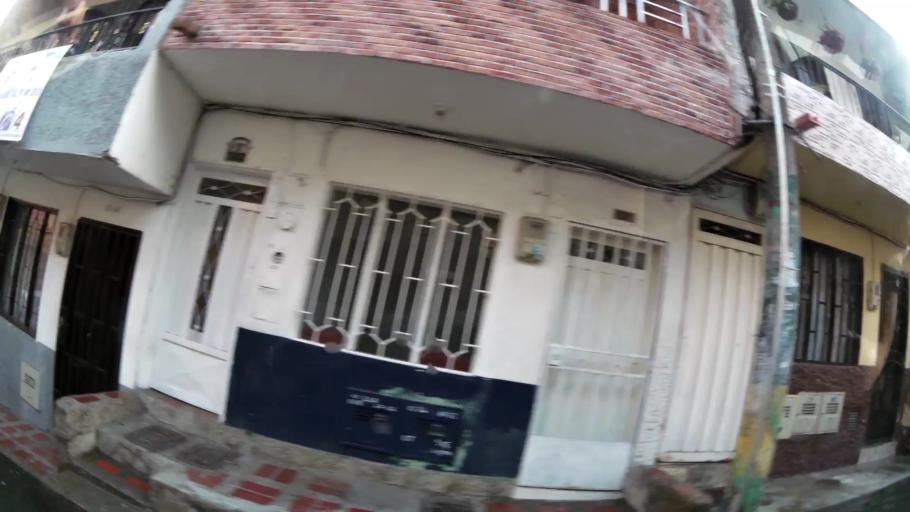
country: CO
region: Antioquia
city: Sabaneta
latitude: 6.1657
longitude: -75.6202
